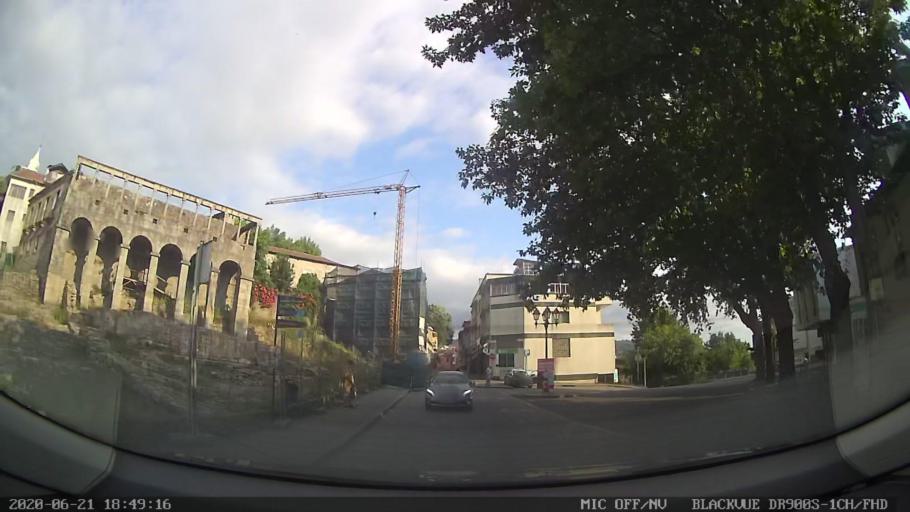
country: PT
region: Porto
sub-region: Amarante
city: Amarante
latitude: 41.2719
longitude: -8.0827
